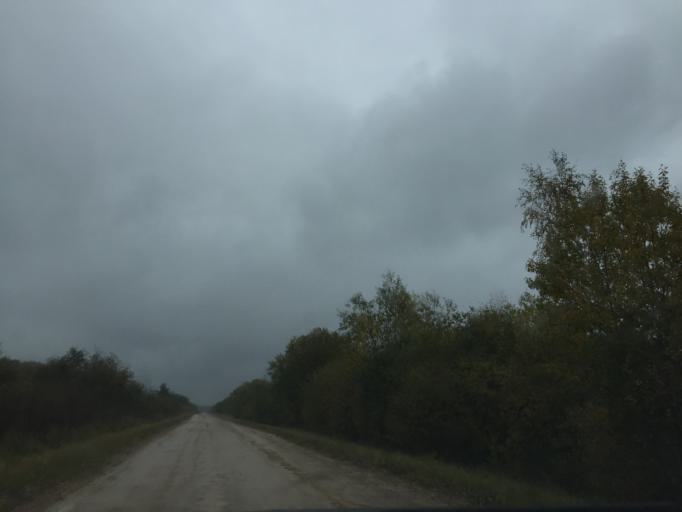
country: LV
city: Tireli
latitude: 56.7436
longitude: 23.5228
